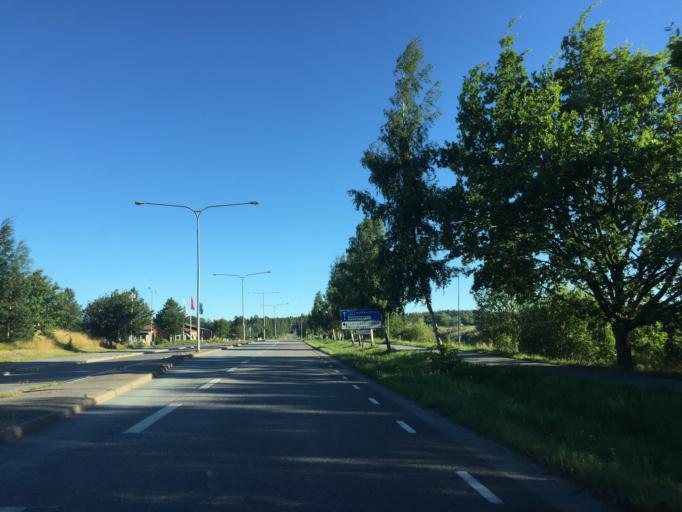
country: SE
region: OErebro
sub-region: Orebro Kommun
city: Orebro
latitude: 59.2568
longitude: 15.1958
